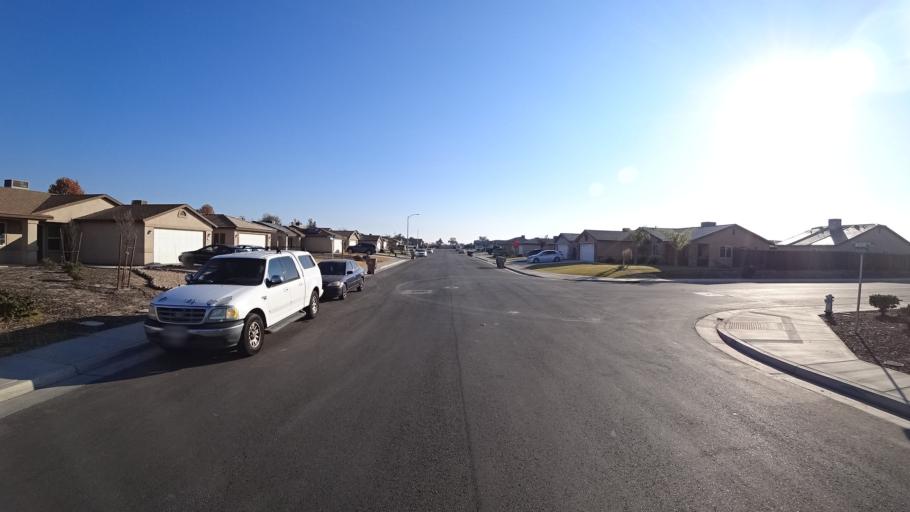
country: US
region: California
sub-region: Kern County
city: Greenfield
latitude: 35.3009
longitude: -119.0077
